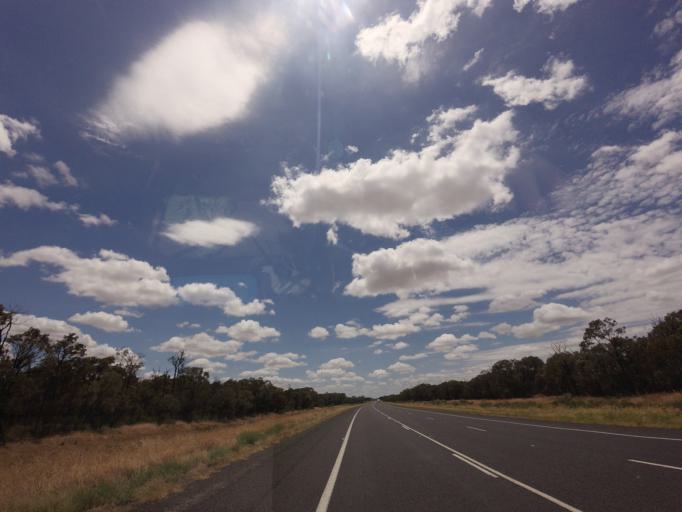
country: AU
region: New South Wales
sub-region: Moree Plains
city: Boggabilla
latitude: -28.8718
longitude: 150.1767
